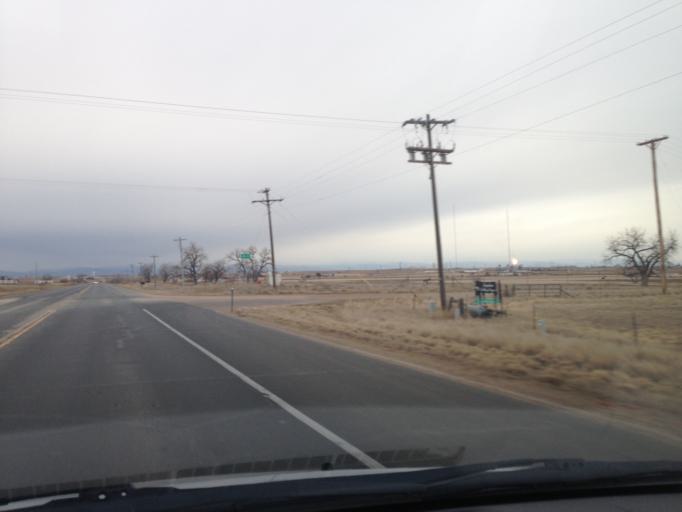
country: US
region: Colorado
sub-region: Weld County
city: Fort Lupton
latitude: 40.0800
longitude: -104.8666
